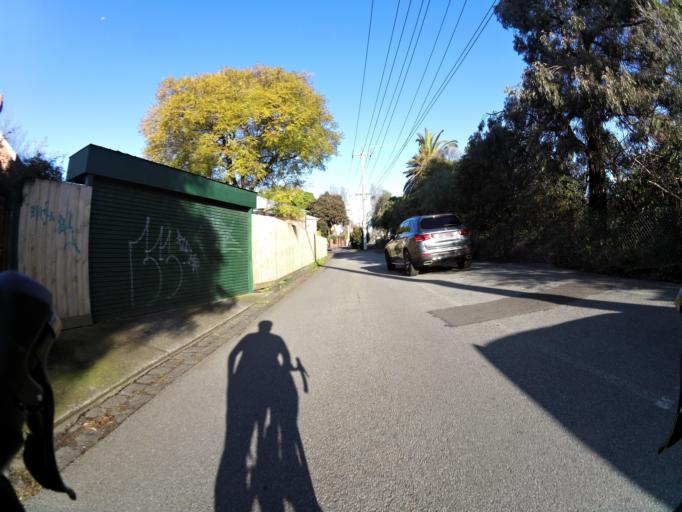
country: AU
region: Victoria
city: Toorak
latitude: -37.8566
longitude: 145.0199
